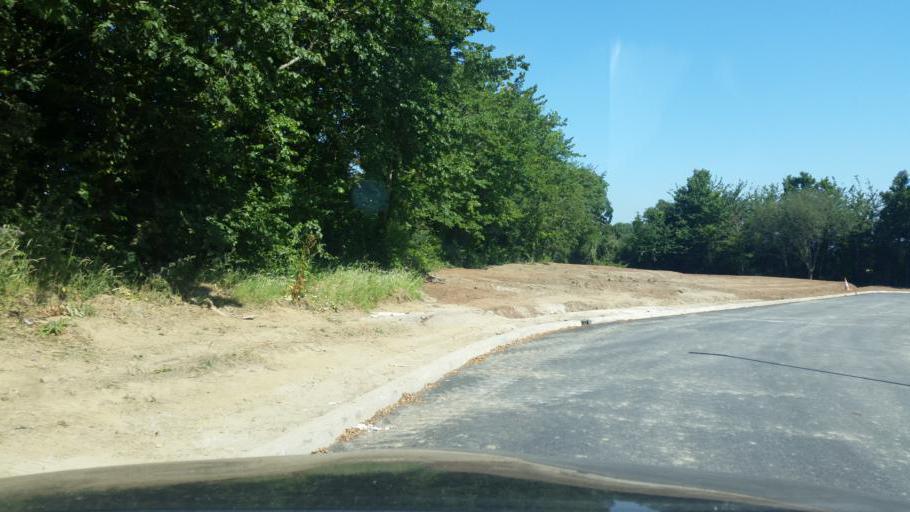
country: IE
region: Leinster
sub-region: Fingal County
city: Swords
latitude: 53.4509
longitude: -6.2530
